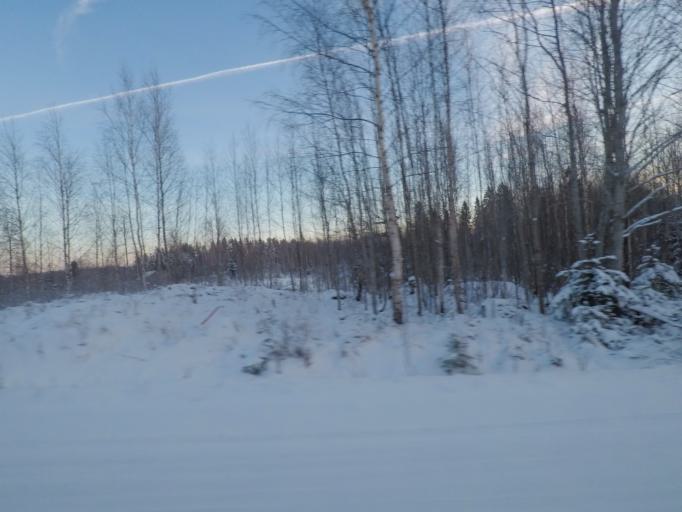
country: FI
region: Varsinais-Suomi
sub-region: Salo
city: Suomusjaervi
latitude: 60.3008
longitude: 23.6432
